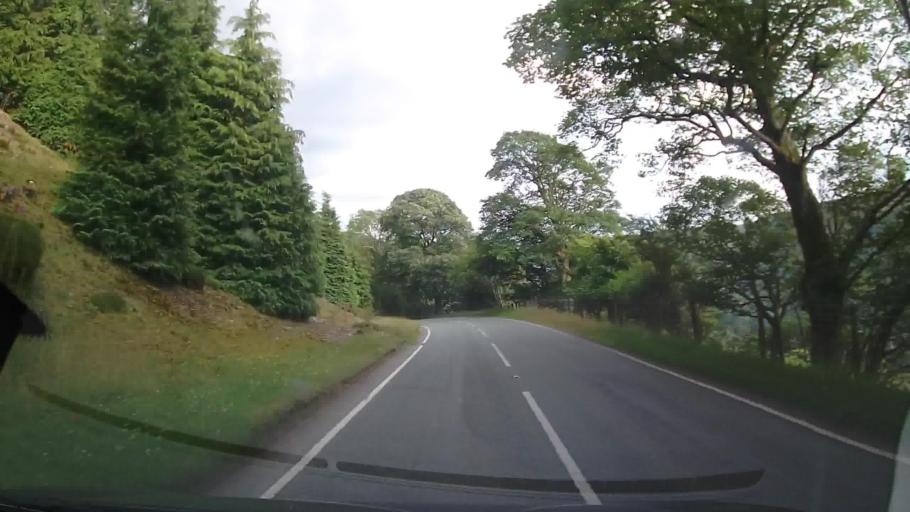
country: GB
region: Wales
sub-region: Sir Powys
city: Llangynog
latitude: 52.8496
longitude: -3.4329
